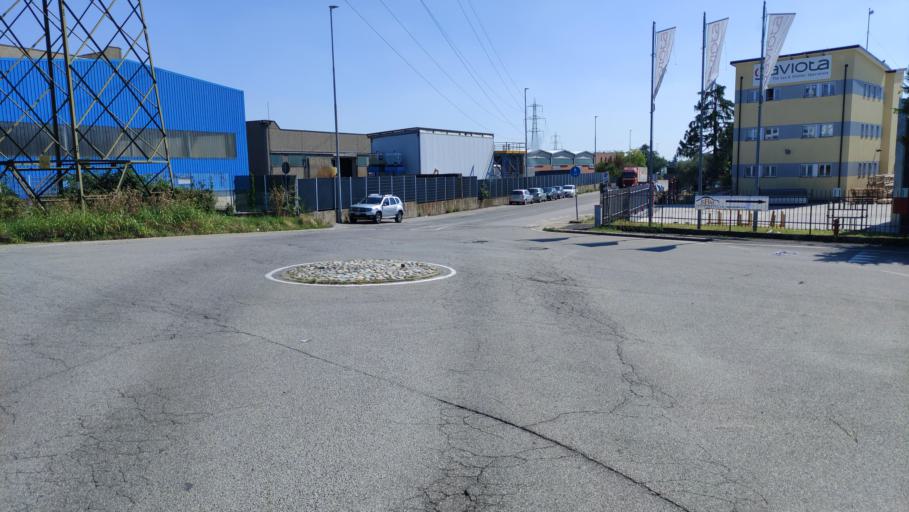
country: IT
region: Lombardy
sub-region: Provincia di Monza e Brianza
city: Mezzago
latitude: 45.6149
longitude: 9.4393
